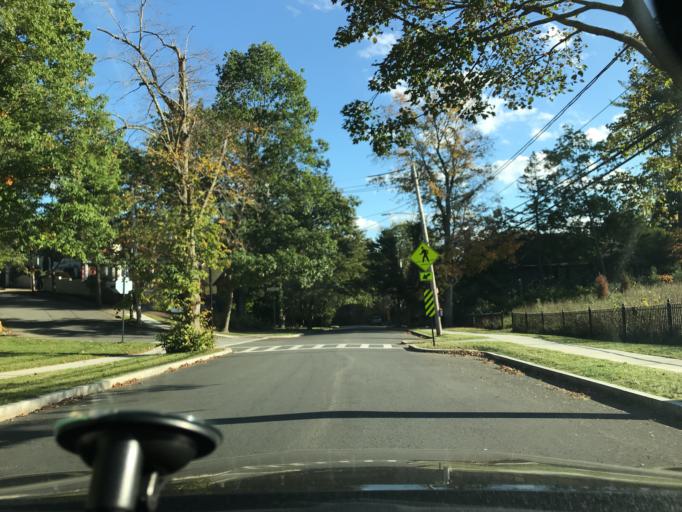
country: US
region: Massachusetts
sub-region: Norfolk County
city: Brookline
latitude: 42.3292
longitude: -71.1419
